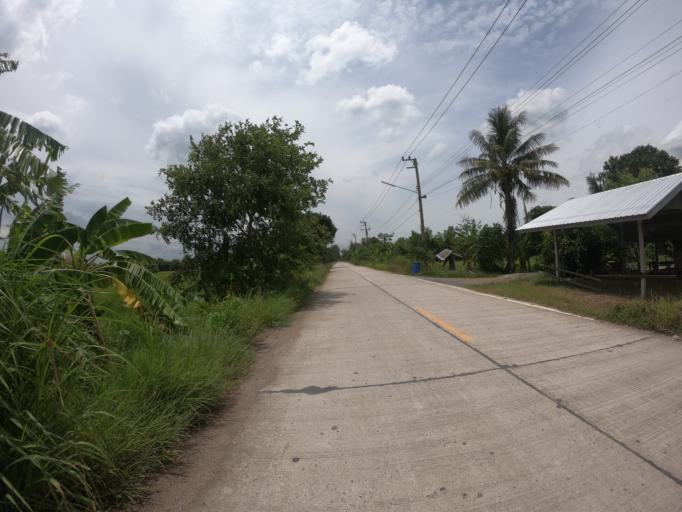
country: TH
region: Pathum Thani
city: Ban Lam Luk Ka
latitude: 14.0294
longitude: 100.8659
